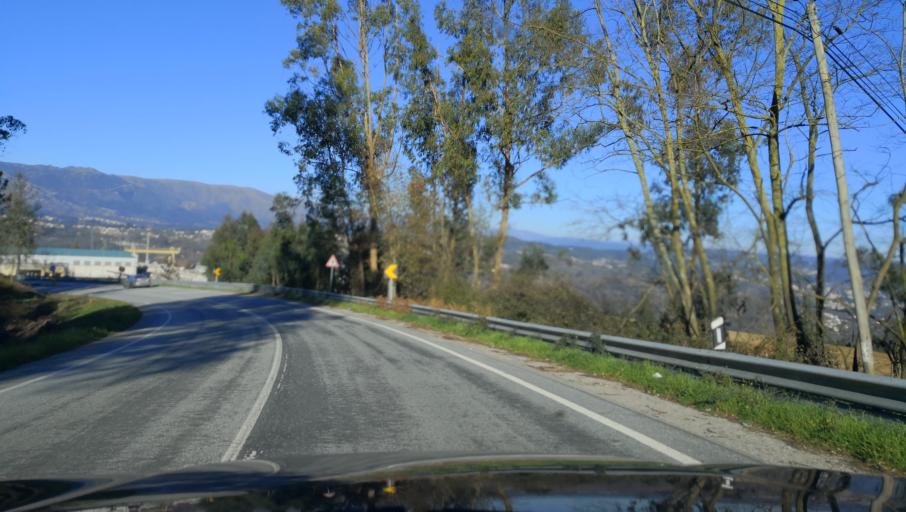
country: PT
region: Viseu
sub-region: Vouzela
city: Vouzela
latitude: 40.7197
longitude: -8.1308
